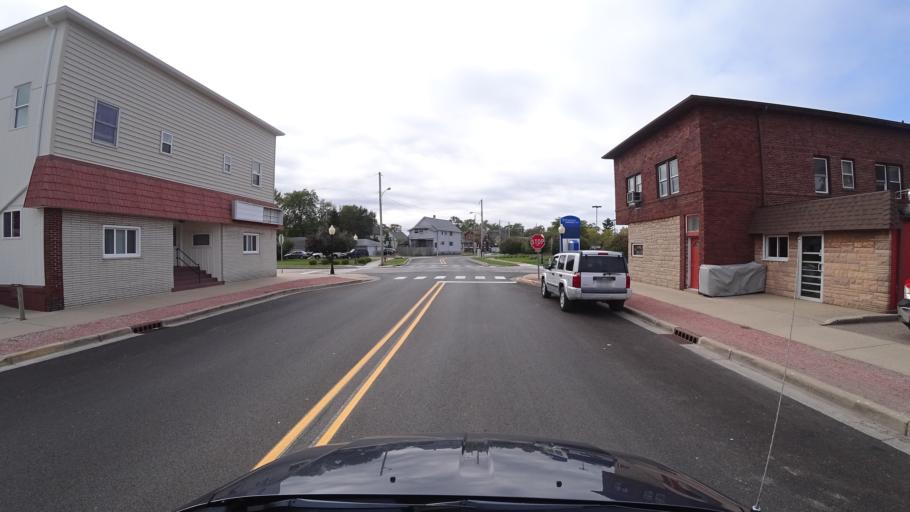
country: US
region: Indiana
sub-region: LaPorte County
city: Michigan City
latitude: 41.7049
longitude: -86.8985
